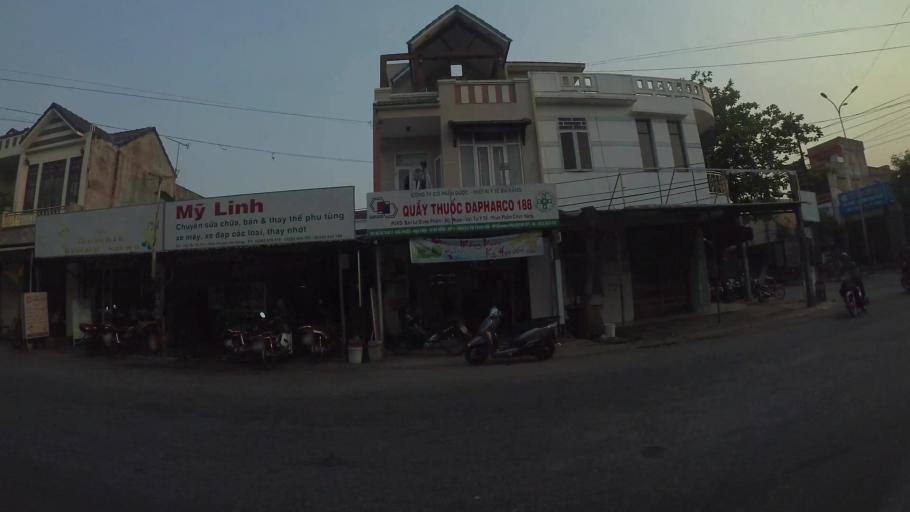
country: VN
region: Quang Nam
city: Quang Nam
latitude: 15.9471
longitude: 108.2207
